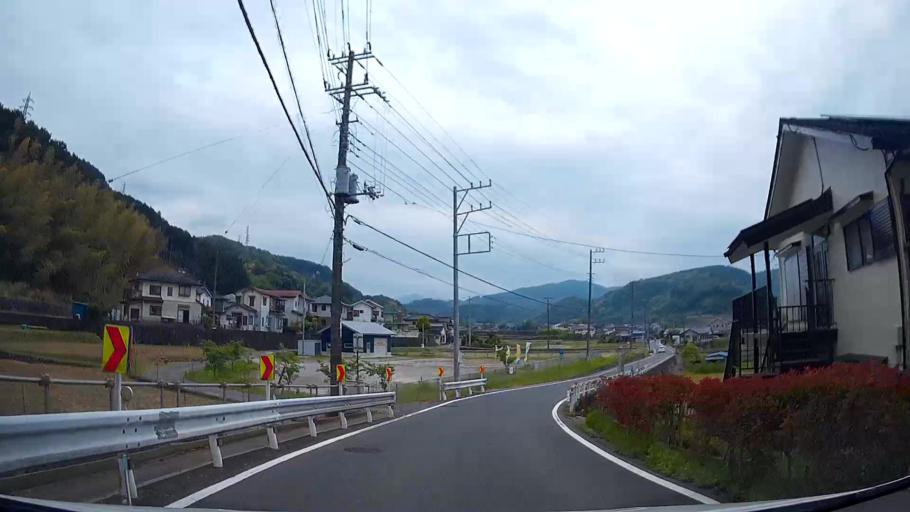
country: JP
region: Shizuoka
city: Ito
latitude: 34.9506
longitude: 138.9423
